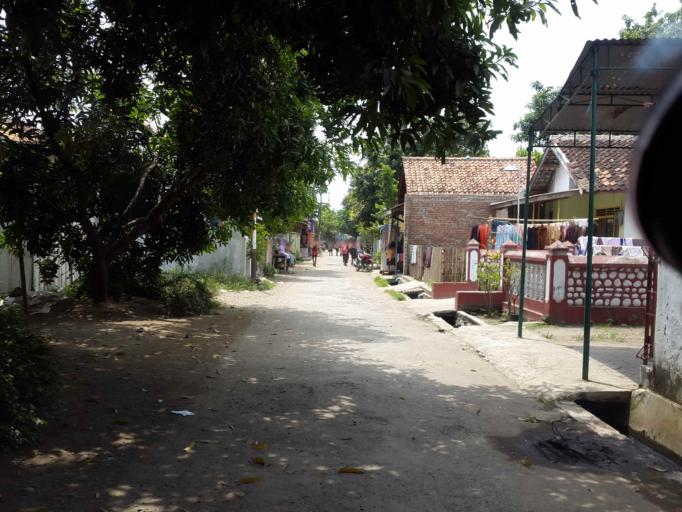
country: ID
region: Central Java
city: Petarukan
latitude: -6.8913
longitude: 109.4112
